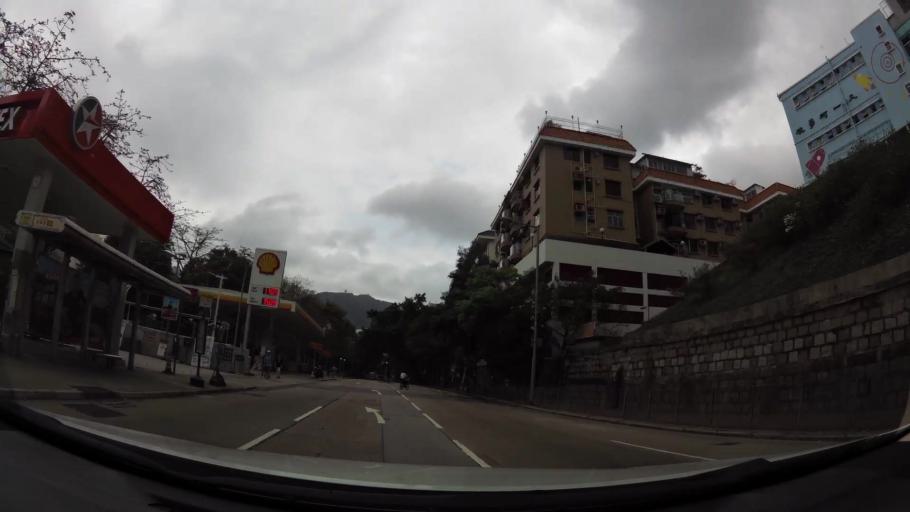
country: HK
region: Sham Shui Po
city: Sham Shui Po
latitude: 22.3278
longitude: 114.1720
